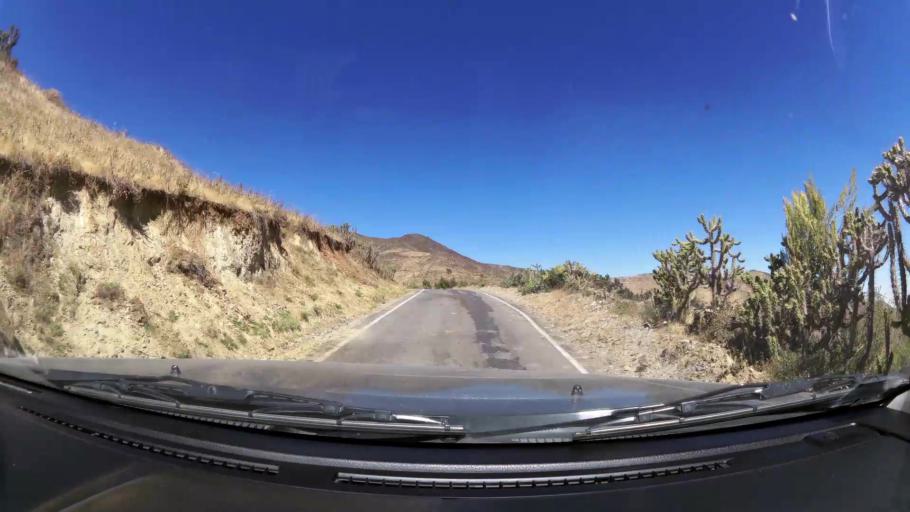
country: PE
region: Huancavelica
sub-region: Huaytara
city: Quito-Arma
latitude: -13.6829
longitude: -75.3770
